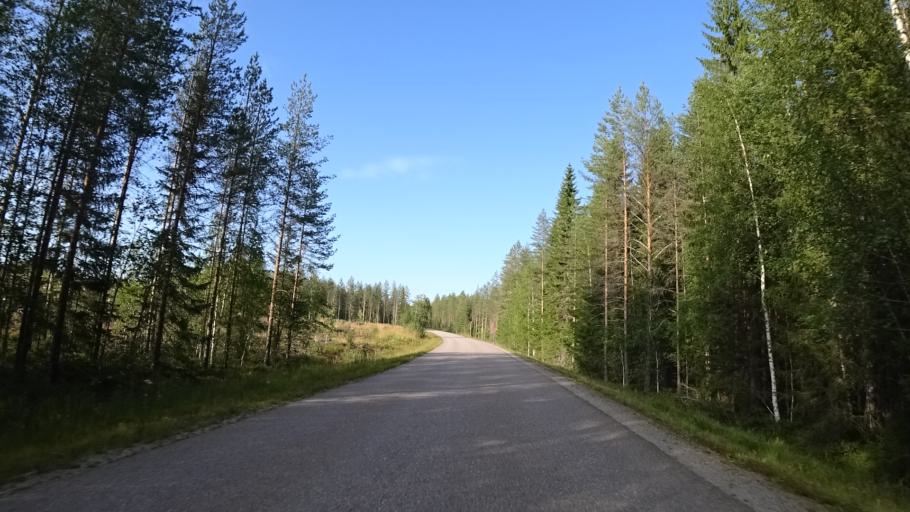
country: FI
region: North Karelia
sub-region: Joensuu
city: Eno
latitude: 63.0319
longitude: 30.5291
